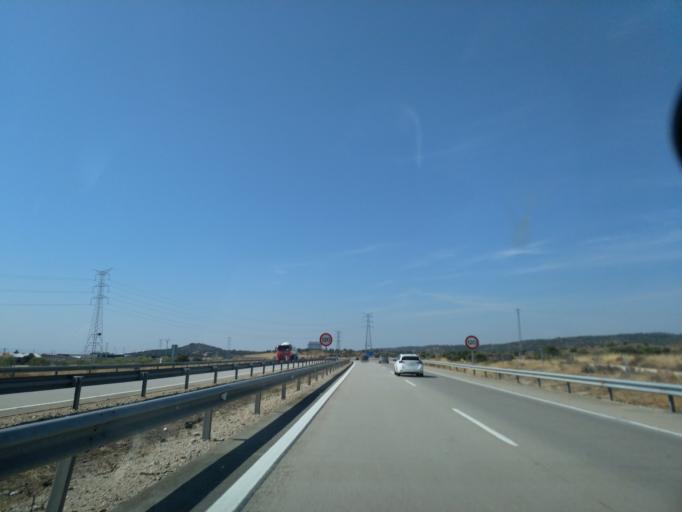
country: ES
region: Castille-La Mancha
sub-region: Province of Toledo
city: Talavera de la Reina
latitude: 40.0053
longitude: -4.8238
